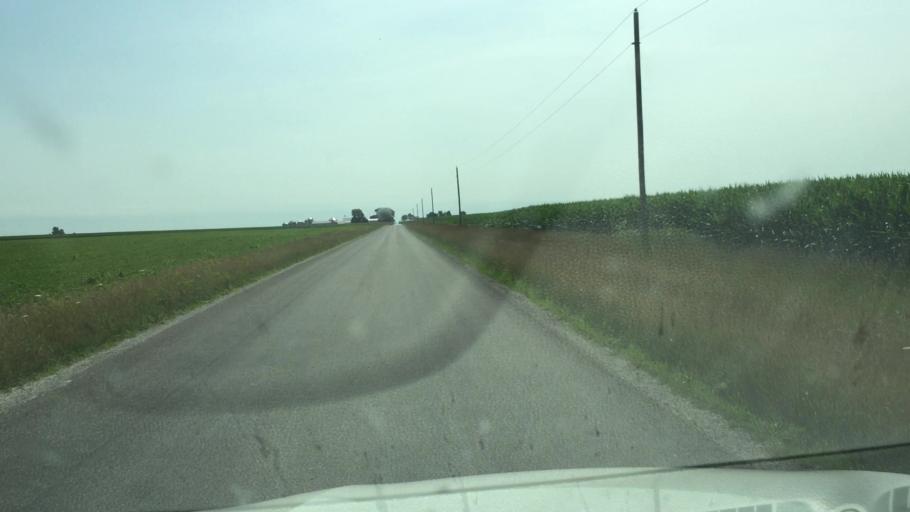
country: US
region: Illinois
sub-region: Hancock County
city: Nauvoo
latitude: 40.5074
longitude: -91.3274
